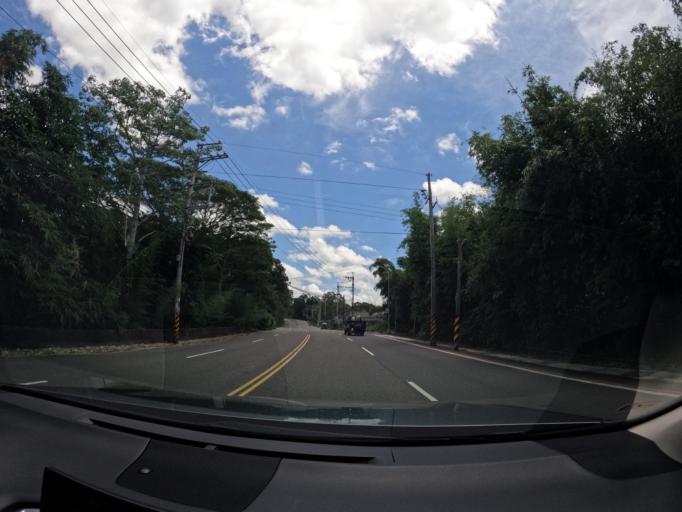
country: TW
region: Taiwan
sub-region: Miaoli
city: Miaoli
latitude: 24.6223
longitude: 120.9523
